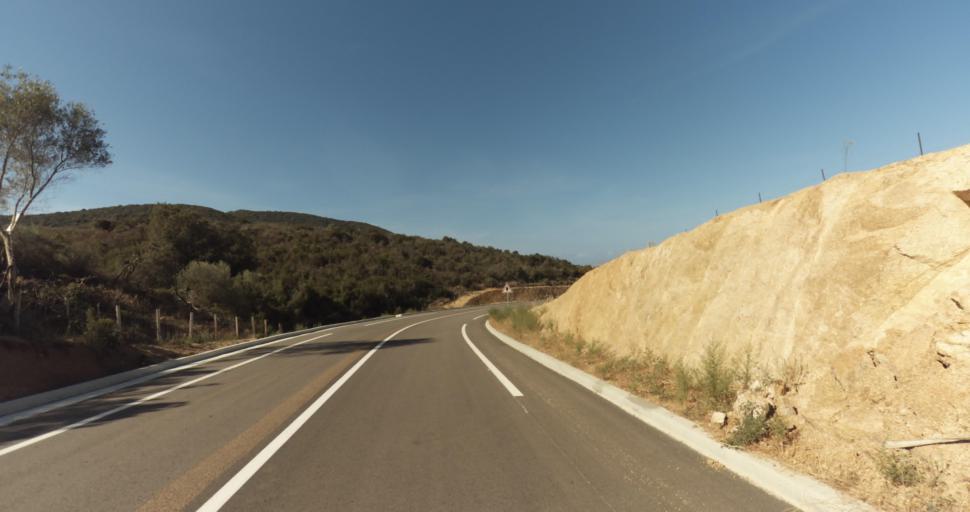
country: FR
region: Corsica
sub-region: Departement de la Corse-du-Sud
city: Ajaccio
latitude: 41.9300
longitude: 8.6505
